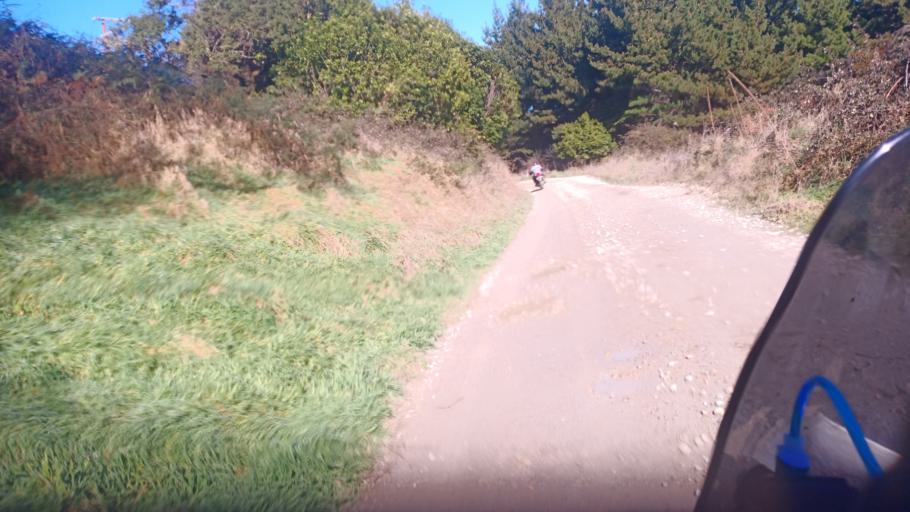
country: NZ
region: Hawke's Bay
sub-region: Wairoa District
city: Wairoa
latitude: -38.6679
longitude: 177.5426
